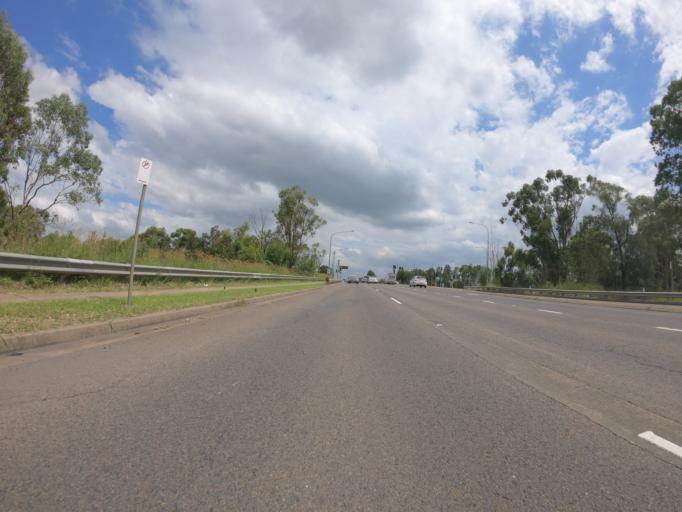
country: AU
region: New South Wales
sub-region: Blacktown
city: Mount Druitt
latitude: -33.7824
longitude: 150.7715
